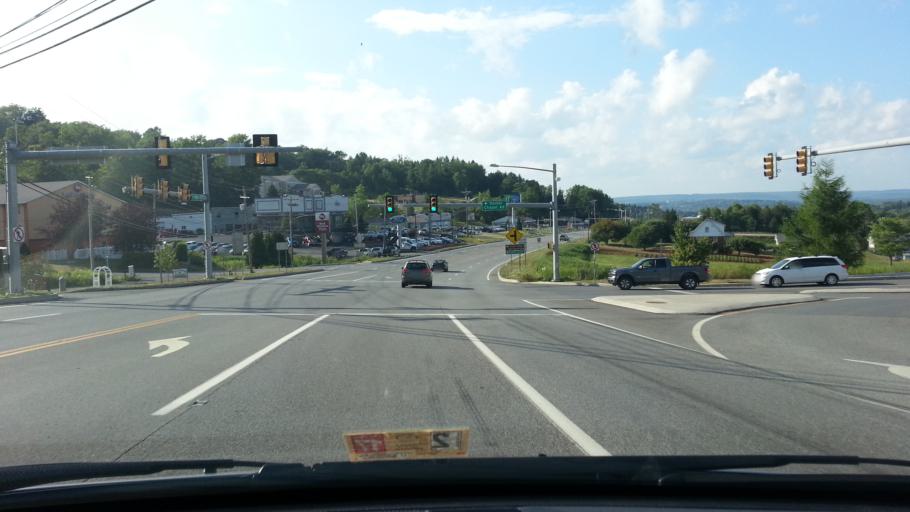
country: US
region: Pennsylvania
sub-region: Elk County
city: Saint Marys
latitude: 41.4005
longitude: -78.5597
